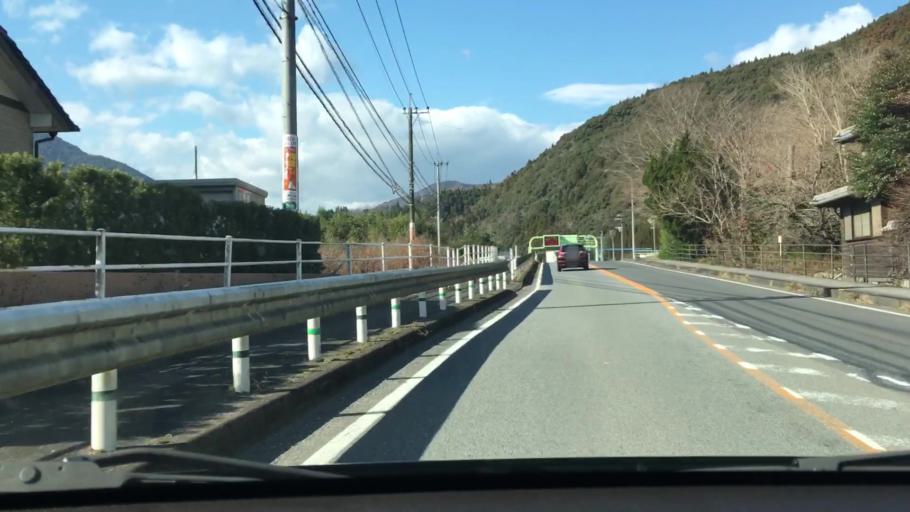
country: JP
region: Oita
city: Saiki
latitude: 32.9864
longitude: 131.8394
